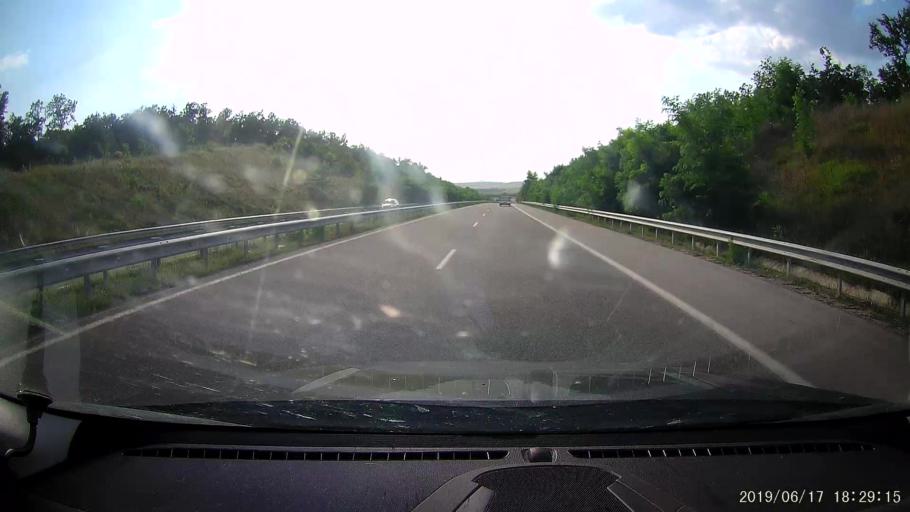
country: BG
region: Khaskovo
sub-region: Obshtina Dimitrovgrad
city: Dimitrovgrad
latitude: 42.0276
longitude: 25.5596
